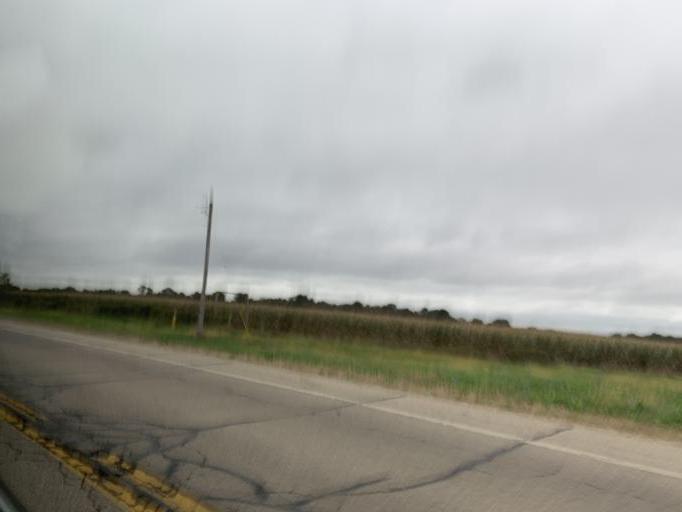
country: US
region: Wisconsin
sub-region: Grant County
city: Muscoda
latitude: 43.2126
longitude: -90.4628
